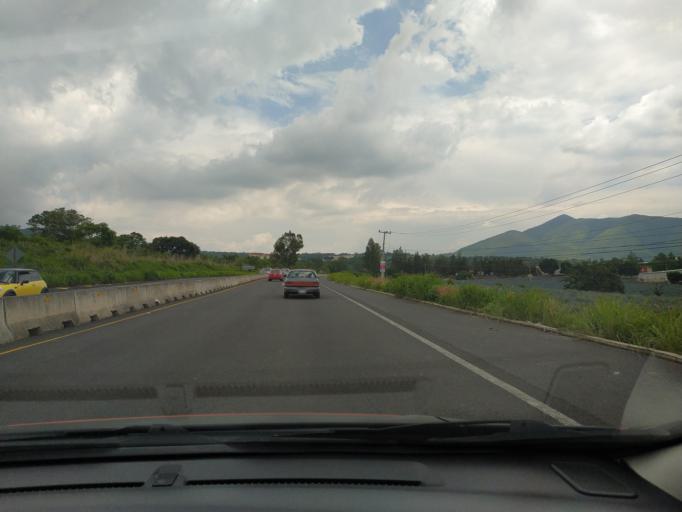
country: MX
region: Jalisco
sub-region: Acatlan de Juarez
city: Villa de los Ninos
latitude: 20.4176
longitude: -103.5491
